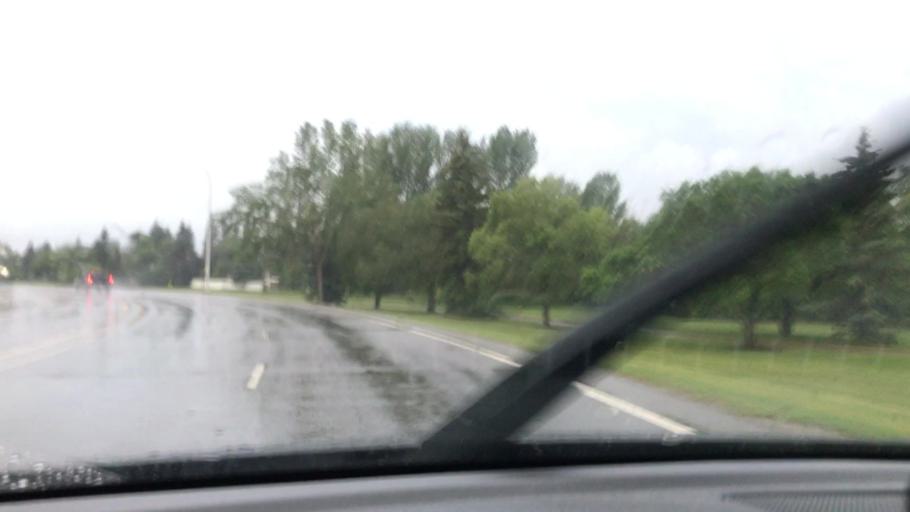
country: CA
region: Alberta
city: Sherwood Park
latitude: 53.5228
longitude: -113.3141
